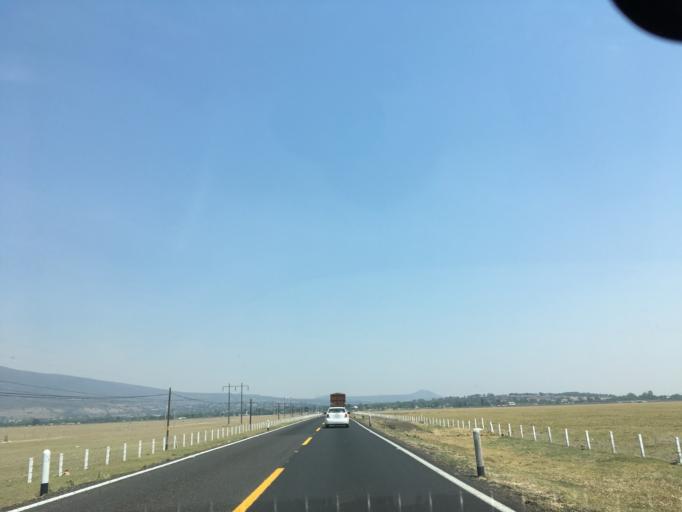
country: MX
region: Michoacan
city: Cuitzeo del Porvenir
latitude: 19.9799
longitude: -101.1438
